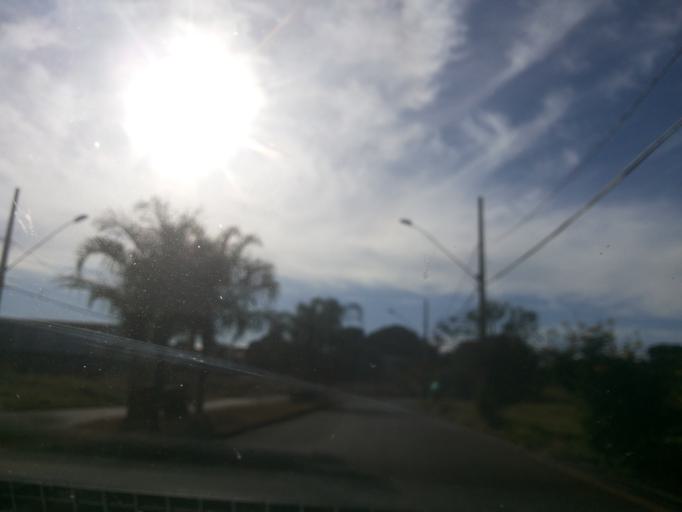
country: BR
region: Minas Gerais
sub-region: Ituiutaba
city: Ituiutaba
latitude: -19.0011
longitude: -49.4589
